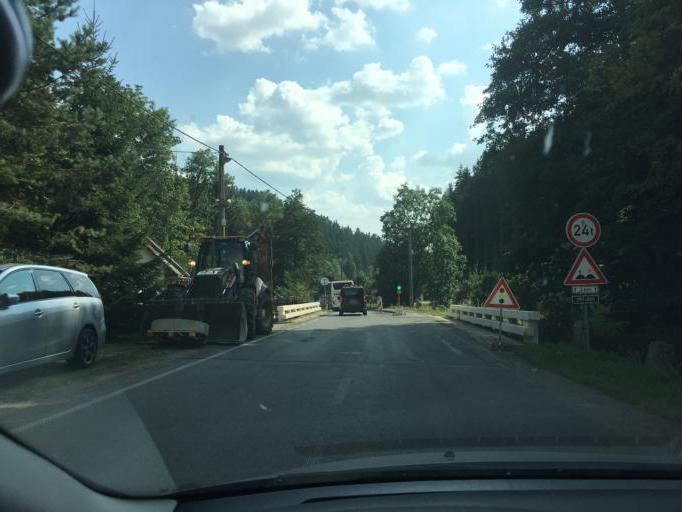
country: CZ
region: Kralovehradecky
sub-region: Okres Trutnov
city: Rudnik
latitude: 50.6287
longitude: 15.7124
